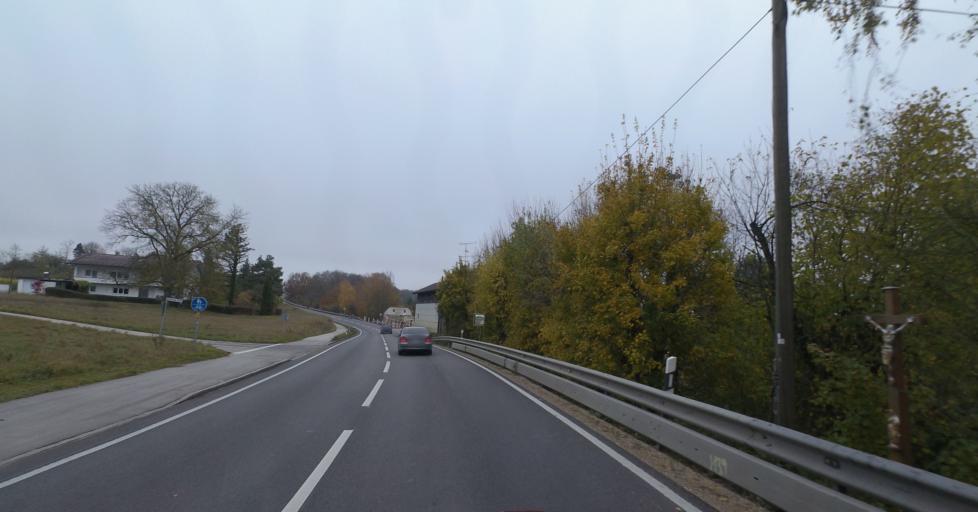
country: DE
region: Bavaria
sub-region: Upper Bavaria
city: Garching an der Alz
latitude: 48.1212
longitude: 12.5756
